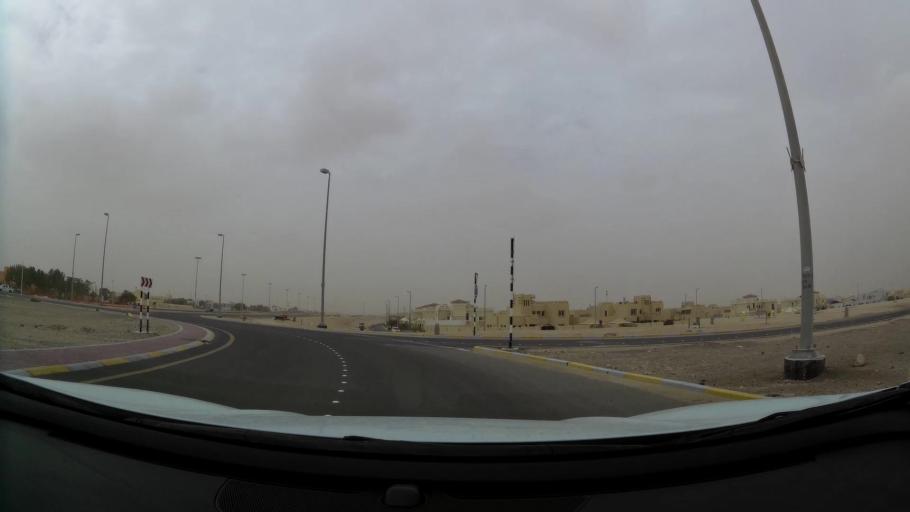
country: AE
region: Abu Dhabi
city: Abu Dhabi
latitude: 24.4305
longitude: 54.7454
